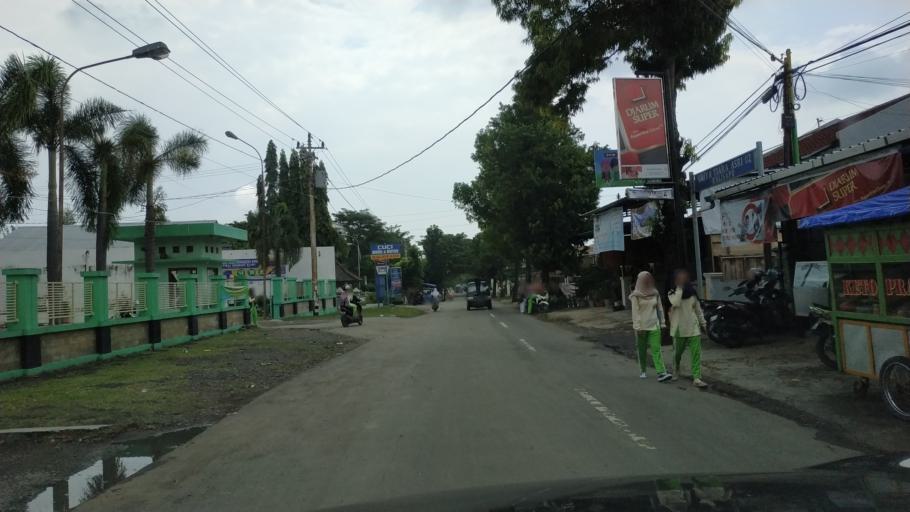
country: ID
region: Central Java
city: Slawi
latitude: -6.9916
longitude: 109.1209
